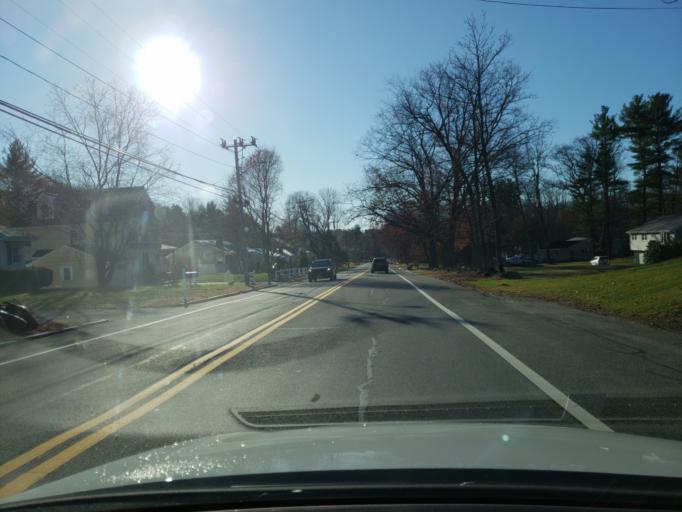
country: US
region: Massachusetts
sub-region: Essex County
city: Andover
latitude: 42.6187
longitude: -71.1251
